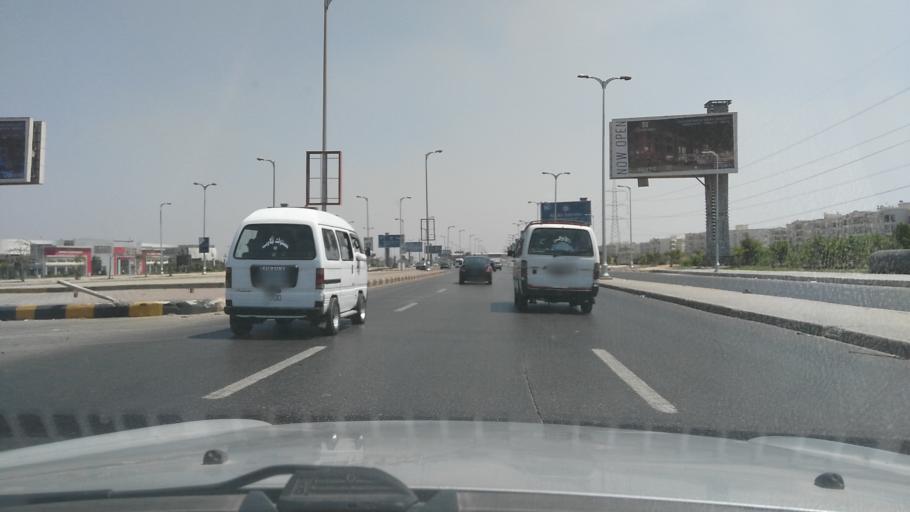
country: EG
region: Al Jizah
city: Awsim
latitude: 30.0236
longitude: 31.0151
